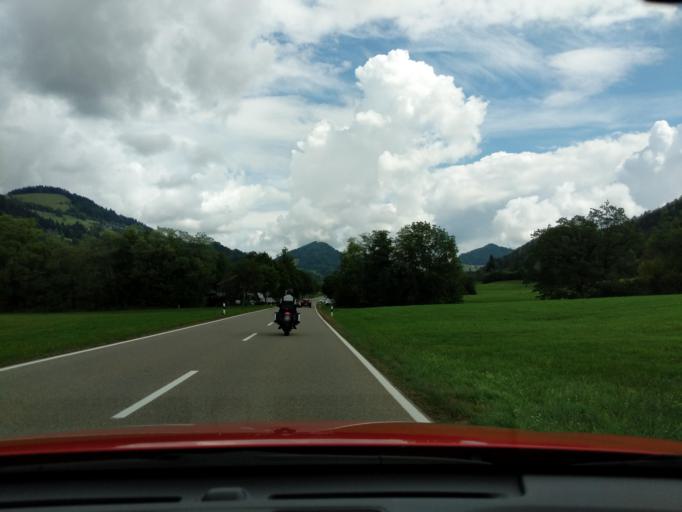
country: AT
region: Vorarlberg
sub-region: Politischer Bezirk Bregenz
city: Riefensberg
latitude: 47.5314
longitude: 9.9878
